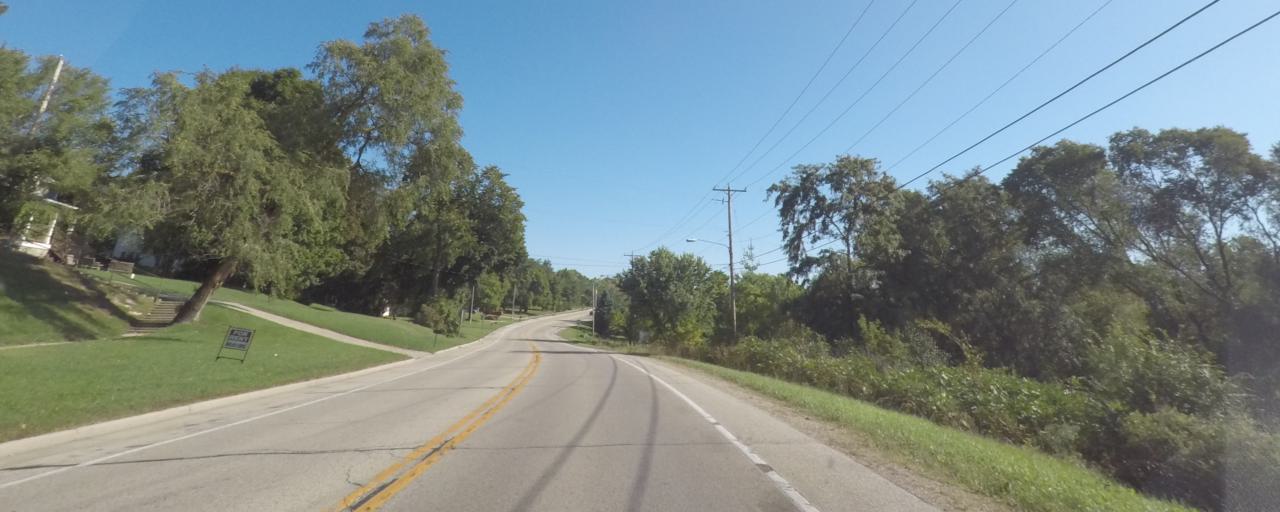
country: US
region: Wisconsin
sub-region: Waukesha County
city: Dousman
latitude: 43.0148
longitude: -88.5859
